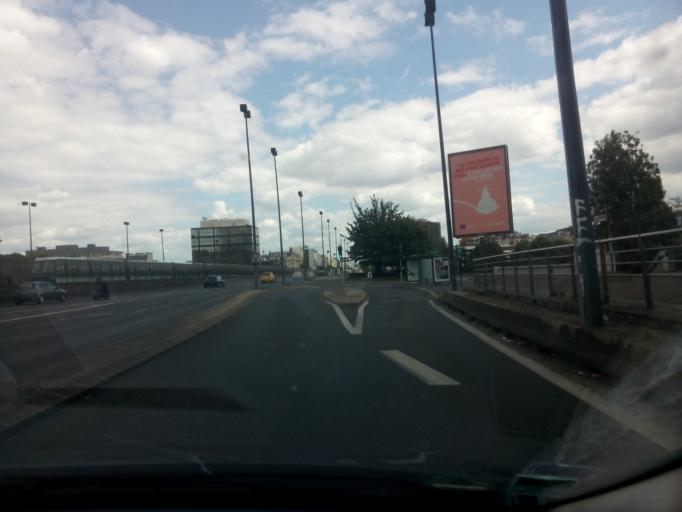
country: FR
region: Ile-de-France
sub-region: Departement des Hauts-de-Seine
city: Courbevoie
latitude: 48.8872
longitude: 2.2512
